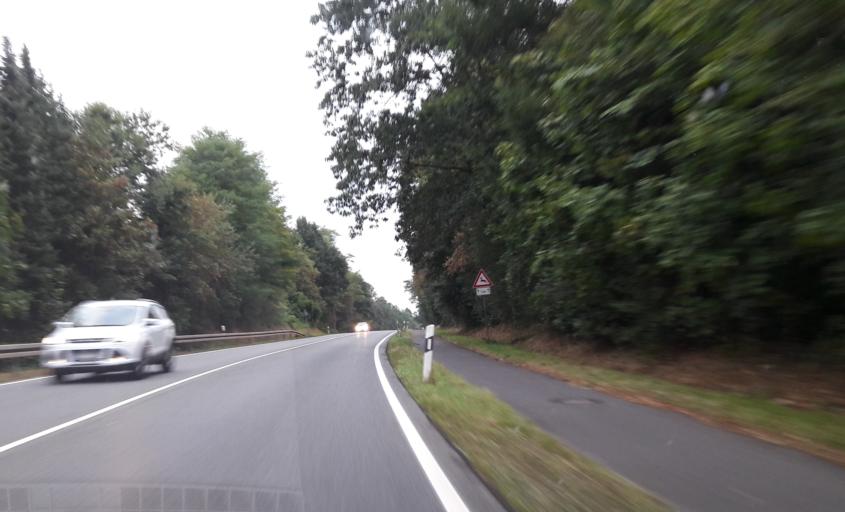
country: DE
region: Saarland
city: Homburg
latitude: 49.2958
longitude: 7.3215
